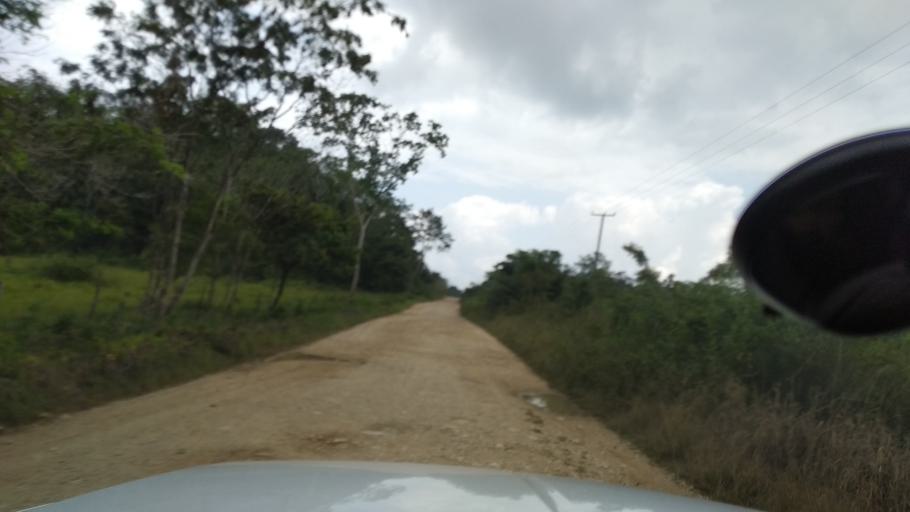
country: BZ
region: Toledo
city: Punta Gorda
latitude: 16.2168
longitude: -89.0053
